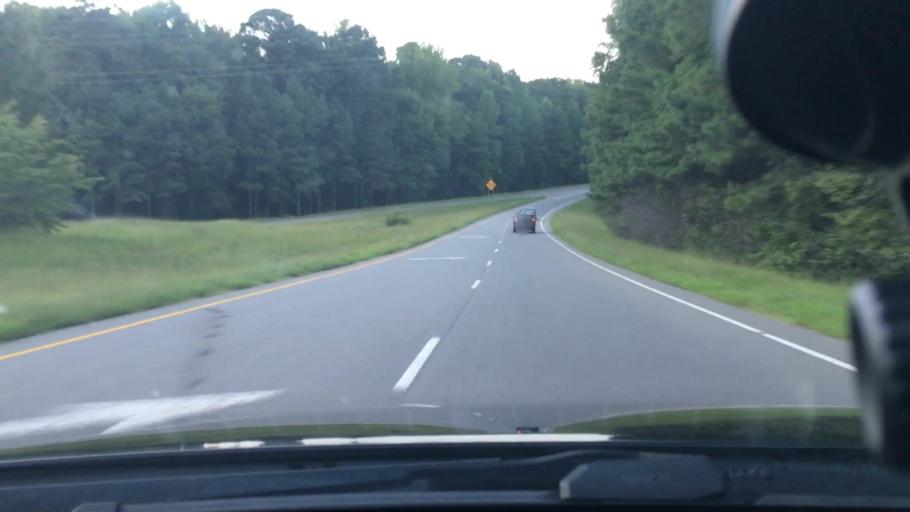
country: US
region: North Carolina
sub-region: Wake County
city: Cary
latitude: 35.7374
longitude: -78.7876
